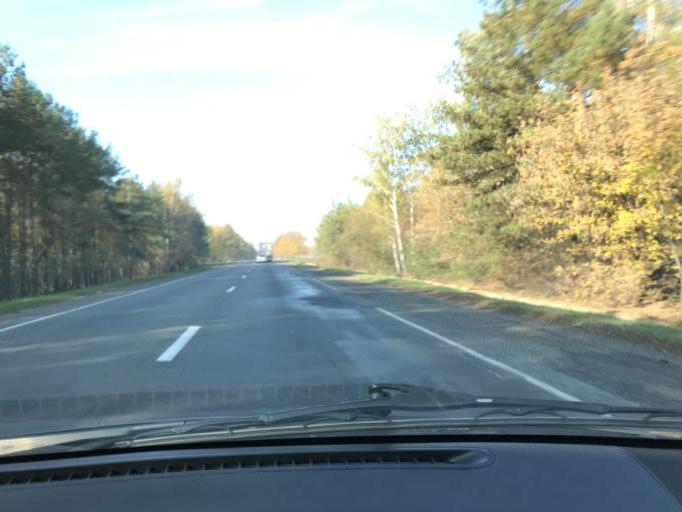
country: BY
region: Brest
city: Luninyets
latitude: 52.2743
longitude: 26.8978
